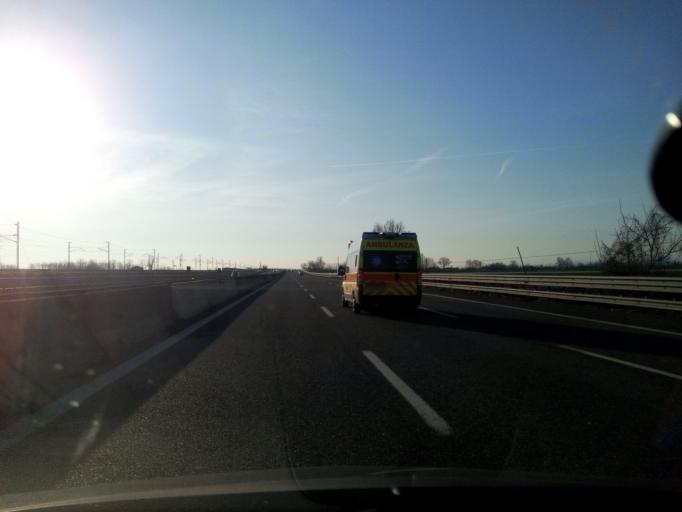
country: IT
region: Emilia-Romagna
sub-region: Provincia di Piacenza
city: Alseno
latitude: 44.9250
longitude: 9.9895
